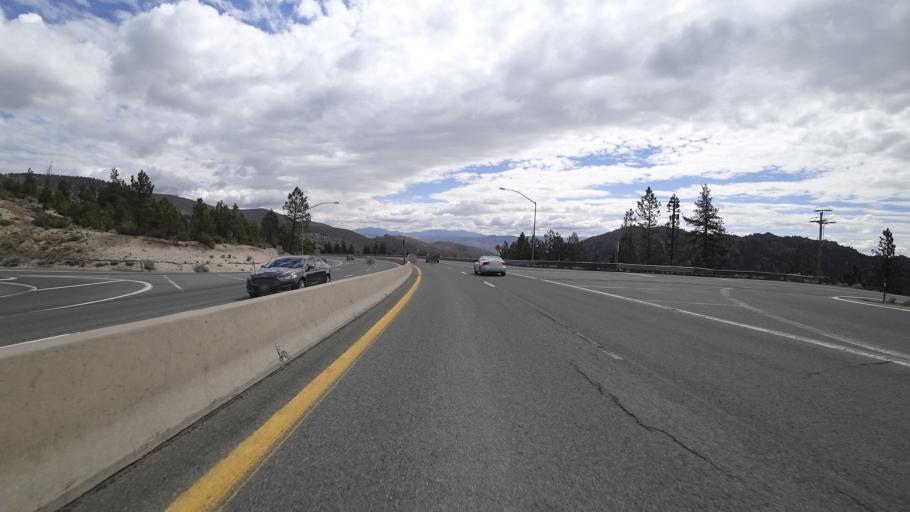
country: US
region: Nevada
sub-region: Douglas County
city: Indian Hills
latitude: 39.1176
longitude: -119.8447
